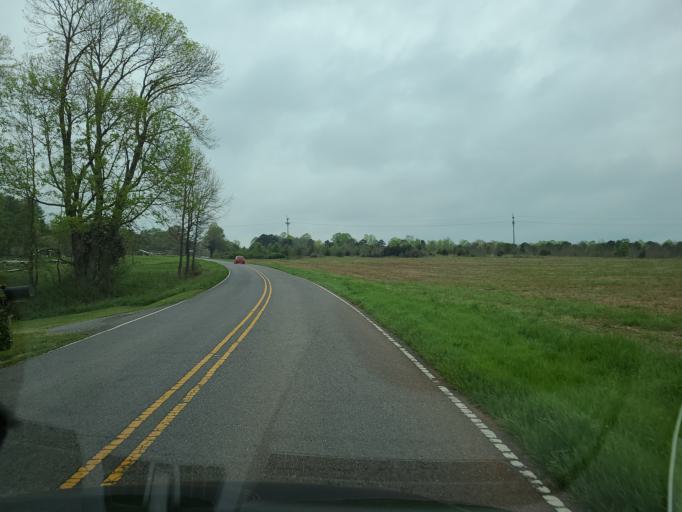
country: US
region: North Carolina
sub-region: Gaston County
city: Cherryville
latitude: 35.4280
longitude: -81.4789
